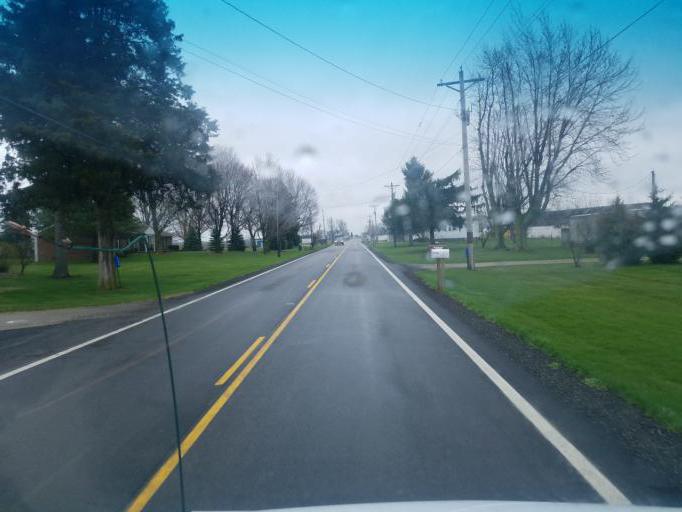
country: US
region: Ohio
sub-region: Huron County
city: Willard
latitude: 40.9605
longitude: -82.8406
